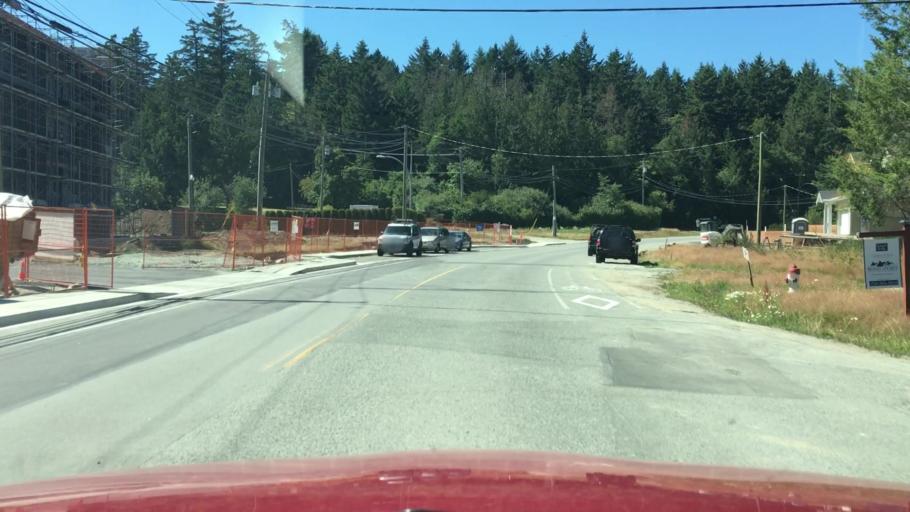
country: CA
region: British Columbia
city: North Saanich
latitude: 48.6718
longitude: -123.4227
